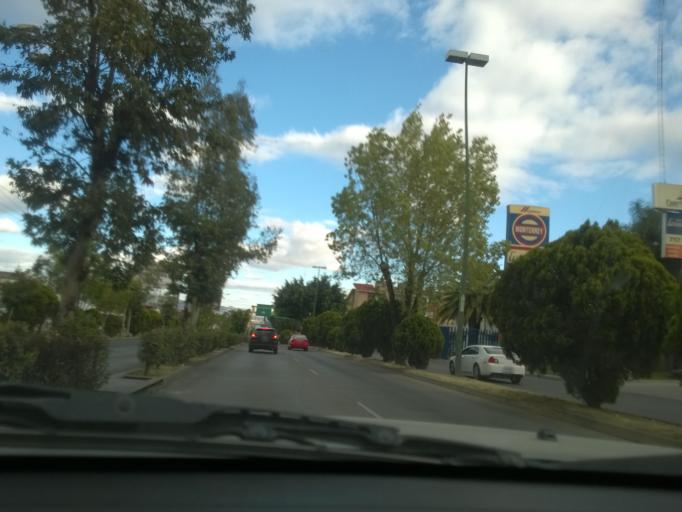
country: MX
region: Guanajuato
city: Leon
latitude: 21.1442
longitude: -101.6952
